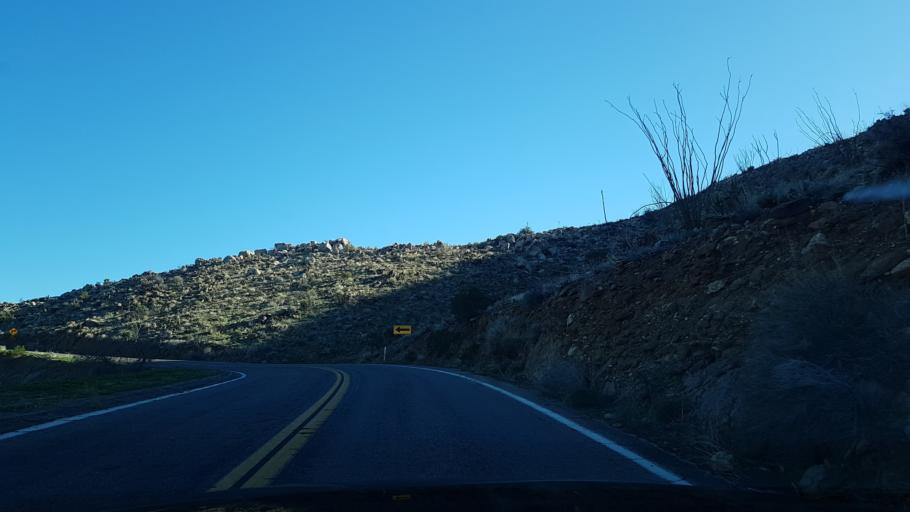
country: US
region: California
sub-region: San Diego County
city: Julian
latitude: 33.0408
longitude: -116.4118
